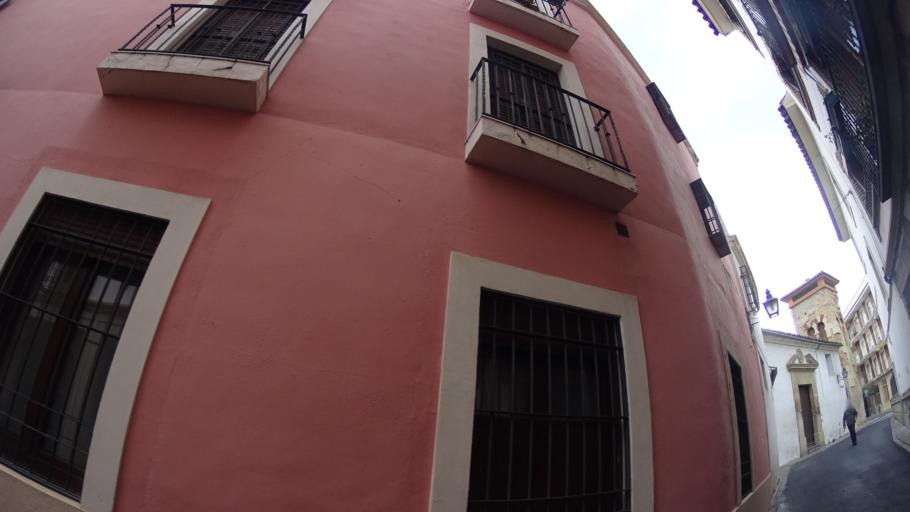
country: ES
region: Andalusia
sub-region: Province of Cordoba
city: Cordoba
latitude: 37.8825
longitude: -4.7811
